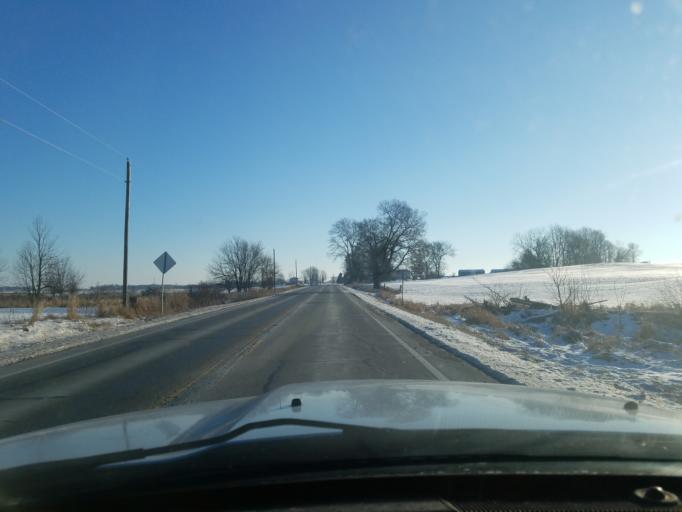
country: US
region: Indiana
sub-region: Noble County
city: Ligonier
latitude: 41.4571
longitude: -85.5043
